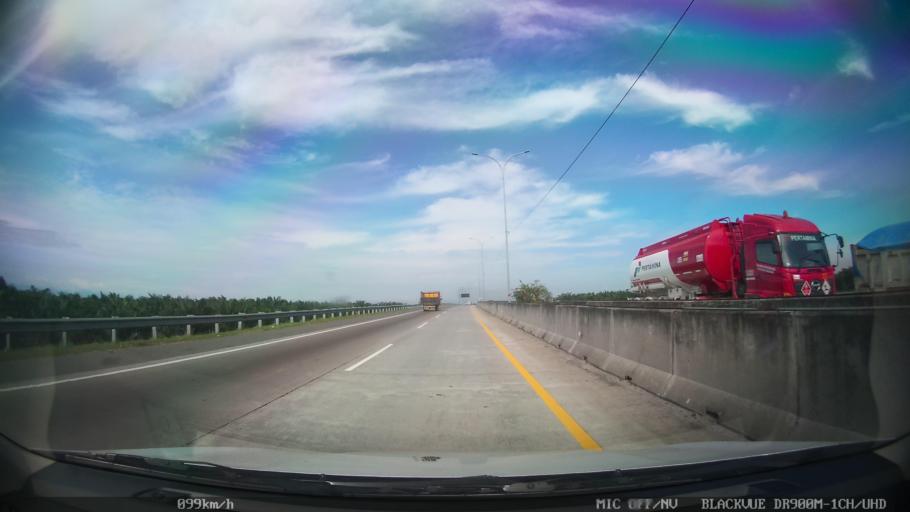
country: ID
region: North Sumatra
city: Sunggal
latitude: 3.6372
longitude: 98.5883
